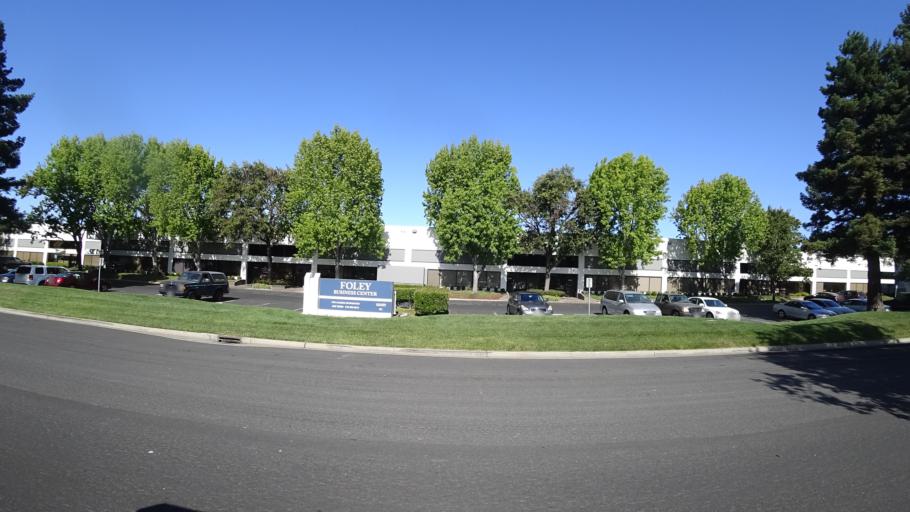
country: US
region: California
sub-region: Alameda County
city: San Lorenzo
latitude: 37.6405
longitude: -122.1313
